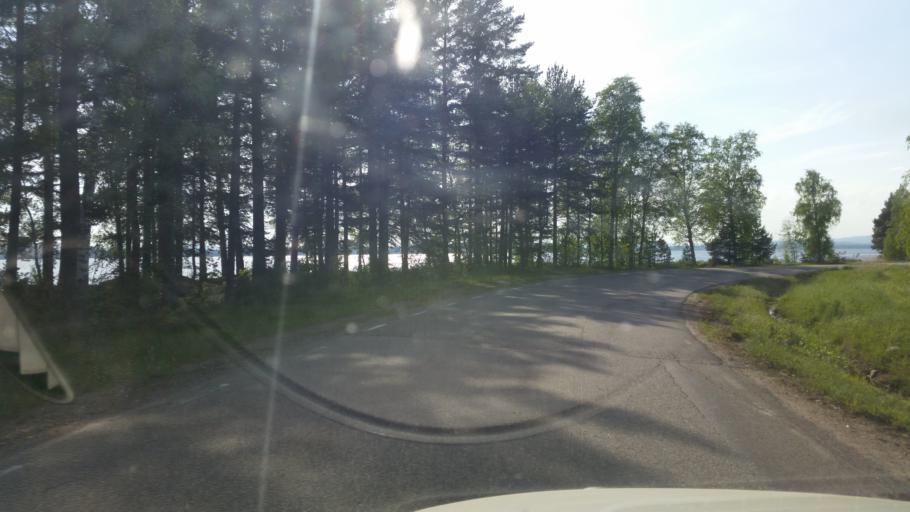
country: SE
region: Gaevleborg
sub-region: Hudiksvalls Kommun
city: Delsbo
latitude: 61.8301
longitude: 16.7256
